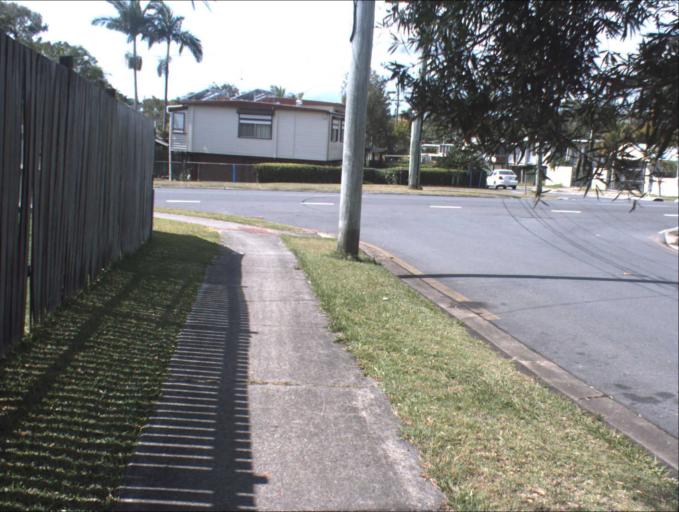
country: AU
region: Queensland
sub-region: Logan
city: Logan City
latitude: -27.6460
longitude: 153.1130
